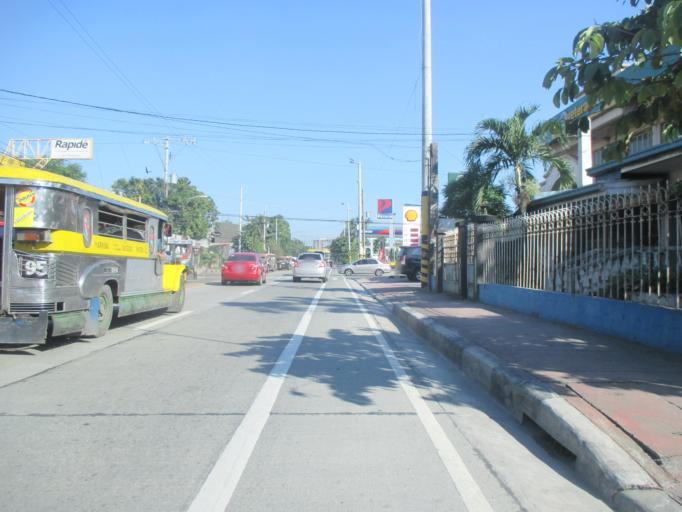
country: PH
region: Metro Manila
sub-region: Marikina
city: Calumpang
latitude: 14.6268
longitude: 121.1022
